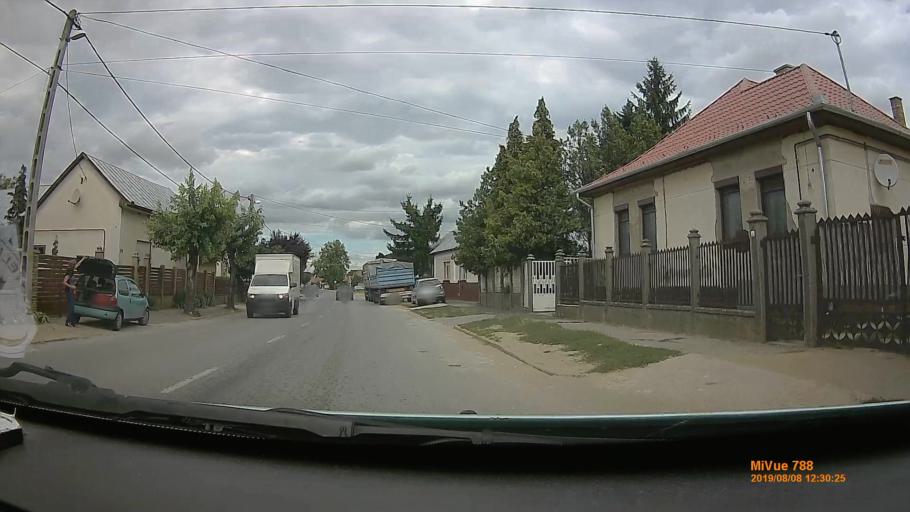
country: HU
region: Szabolcs-Szatmar-Bereg
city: Nyirbator
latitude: 47.8391
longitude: 22.1230
